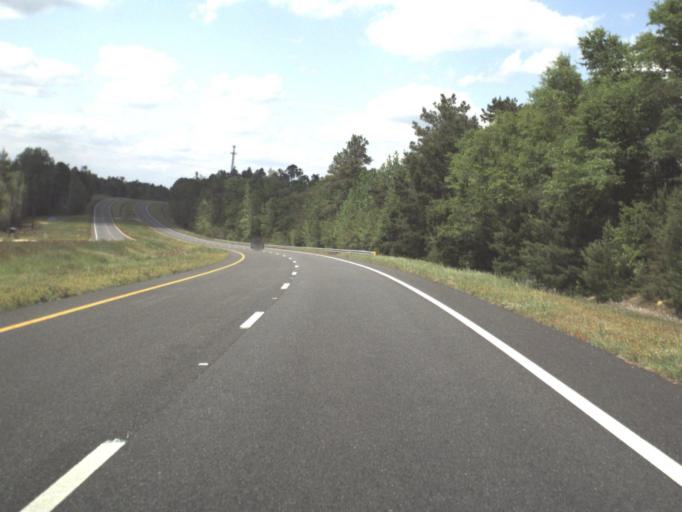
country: US
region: Florida
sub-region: Escambia County
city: Molino
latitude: 30.8486
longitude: -87.3218
